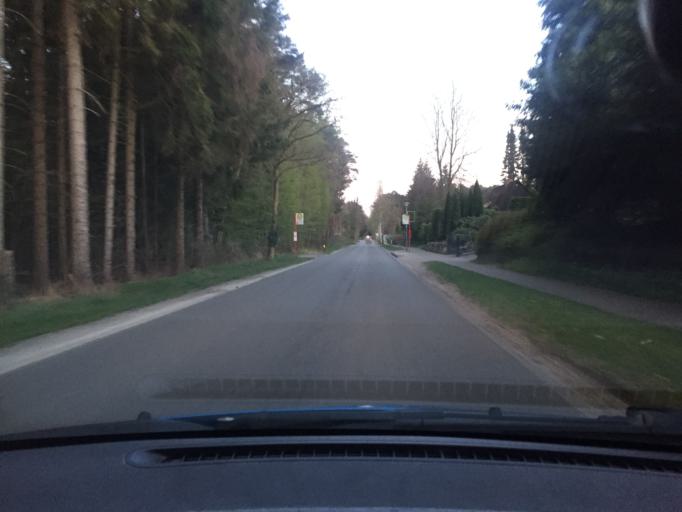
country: DE
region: Lower Saxony
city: Buchholz in der Nordheide
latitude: 53.3084
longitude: 9.8659
